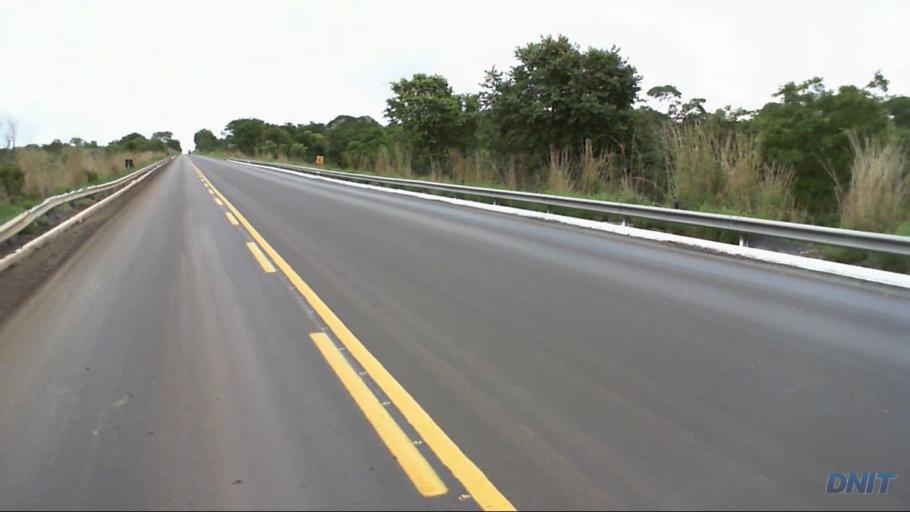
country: BR
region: Goias
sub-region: Padre Bernardo
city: Padre Bernardo
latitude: -15.1772
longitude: -48.4120
